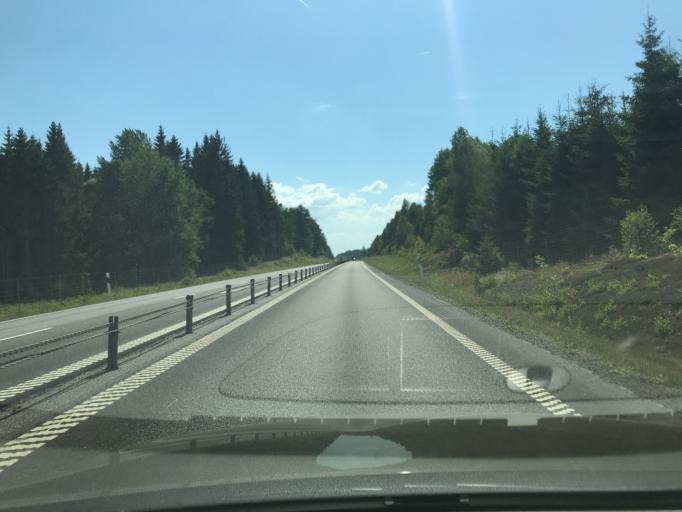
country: SE
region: Kronoberg
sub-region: Almhults Kommun
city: AElmhult
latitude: 56.4567
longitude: 14.0913
